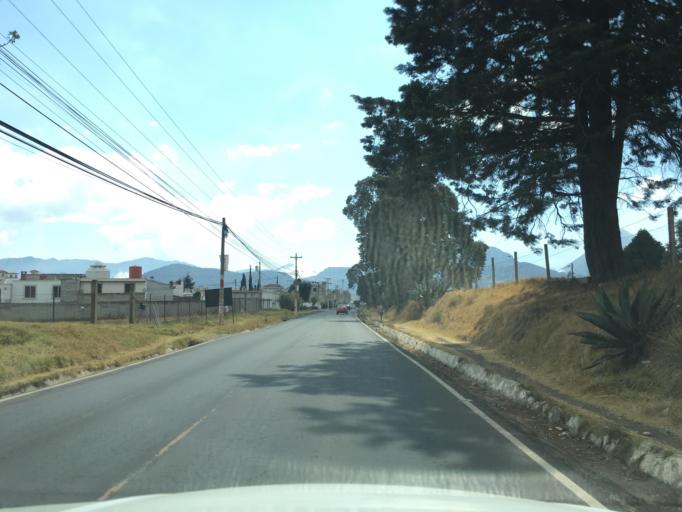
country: GT
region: Quetzaltenango
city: Olintepeque
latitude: 14.8695
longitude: -91.5130
